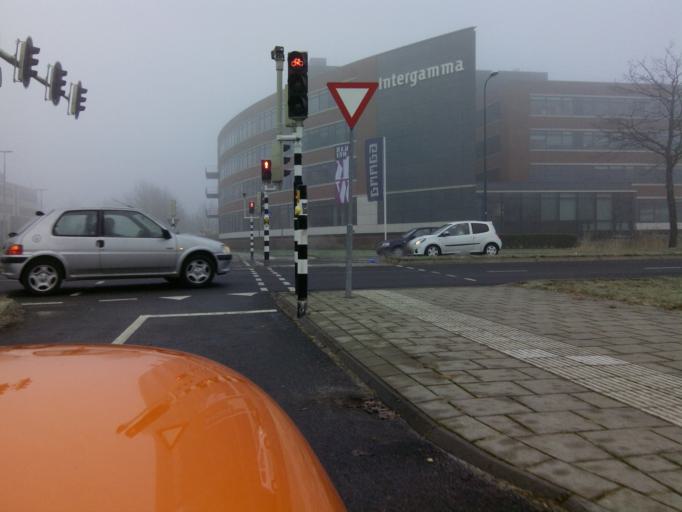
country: NL
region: Utrecht
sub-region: Gemeente Leusden
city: Leusden
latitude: 52.1427
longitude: 5.4202
